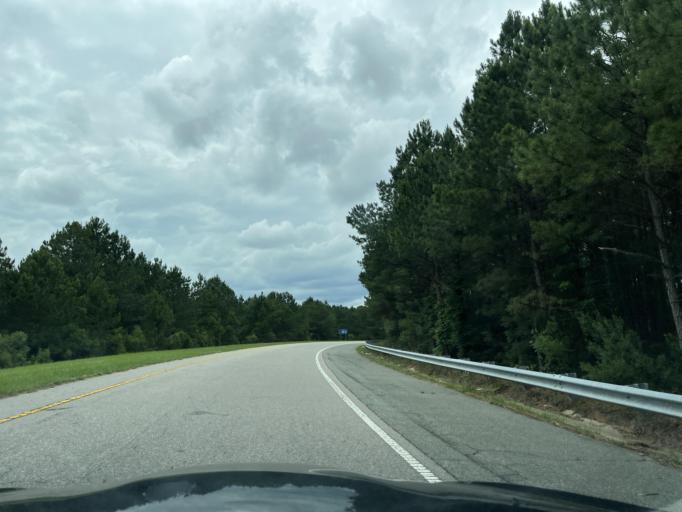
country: US
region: North Carolina
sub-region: Wake County
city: Morrisville
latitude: 35.8949
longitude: -78.8112
